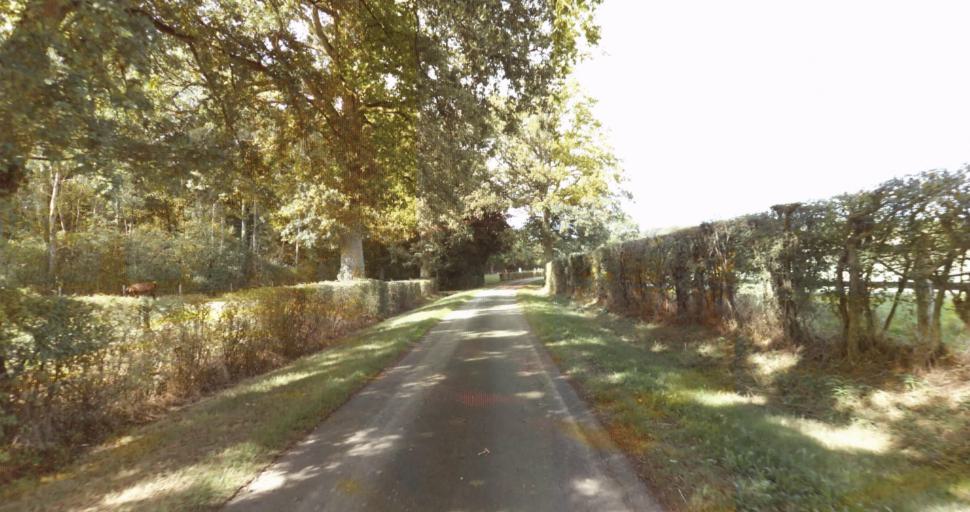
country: FR
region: Lower Normandy
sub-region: Departement de l'Orne
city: Sees
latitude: 48.7029
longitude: 0.1767
